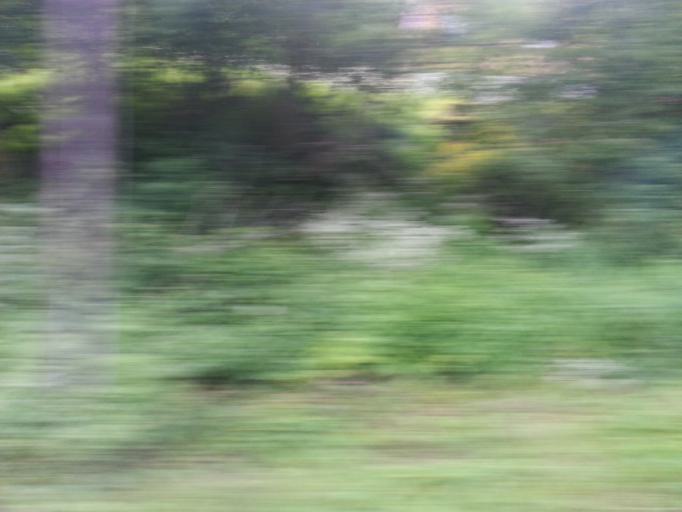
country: NO
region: Sor-Trondelag
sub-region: Malvik
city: Malvik
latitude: 63.4342
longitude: 10.6259
